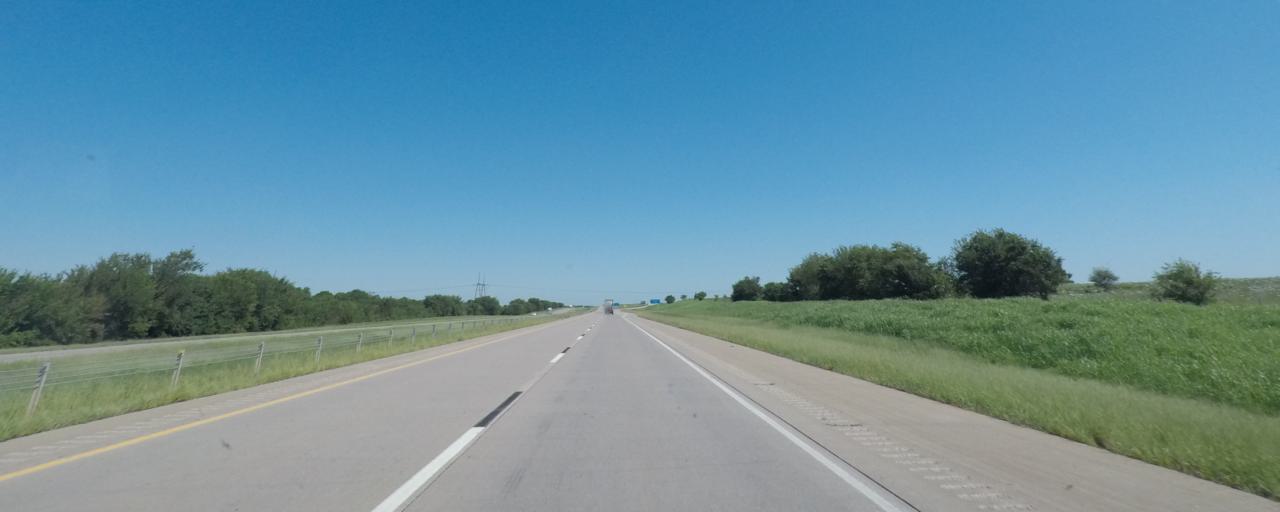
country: US
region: Oklahoma
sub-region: Noble County
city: Perry
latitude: 36.4196
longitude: -97.3268
